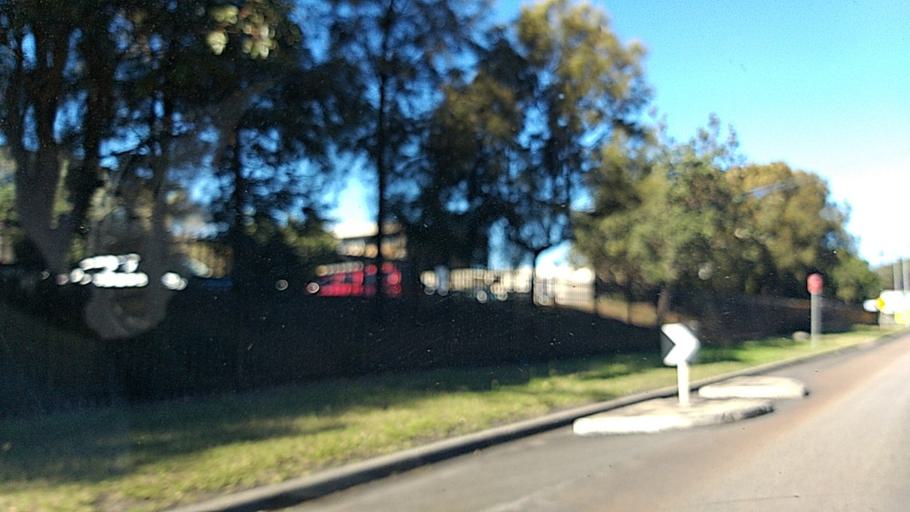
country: AU
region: New South Wales
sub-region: Wollongong
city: Coniston
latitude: -34.4413
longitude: 150.8967
